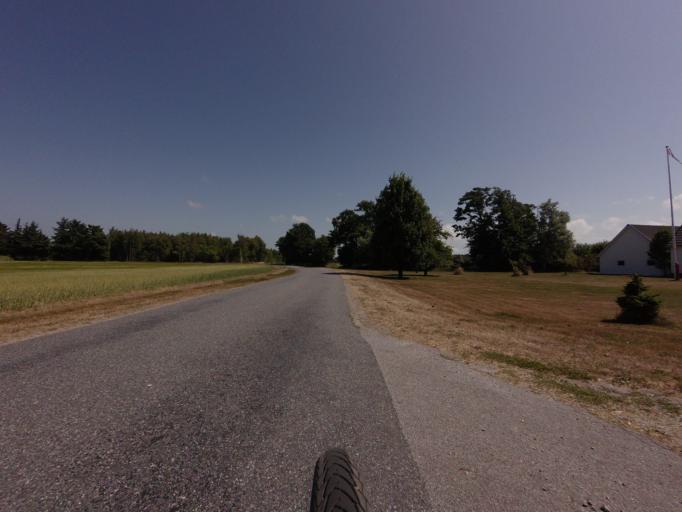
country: DK
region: North Denmark
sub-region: Laeso Kommune
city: Byrum
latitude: 57.2522
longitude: 10.9565
